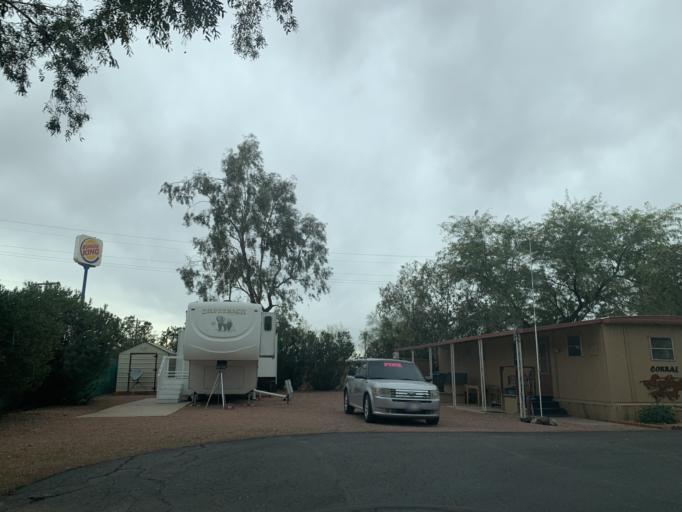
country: US
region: Arizona
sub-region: Pinal County
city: Arizona City
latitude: 32.8144
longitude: -111.6724
